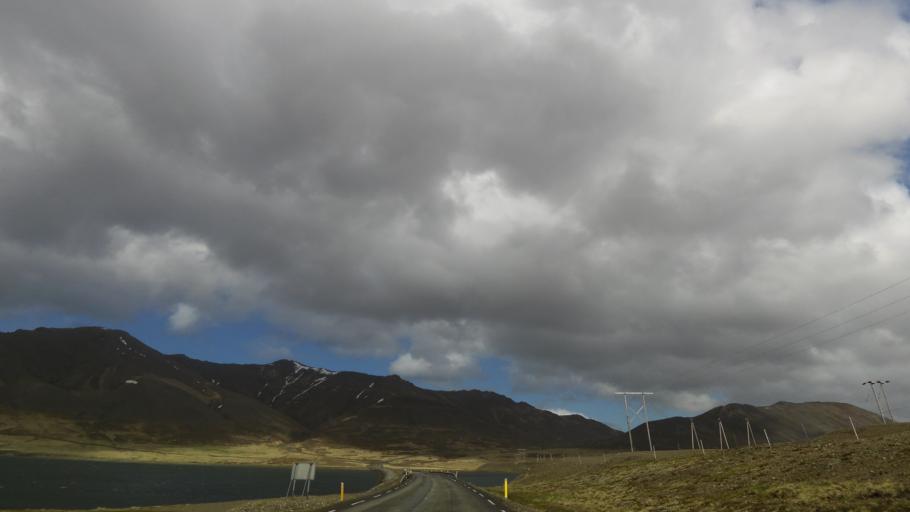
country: IS
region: West
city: Stykkisholmur
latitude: 64.9576
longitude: -23.0326
